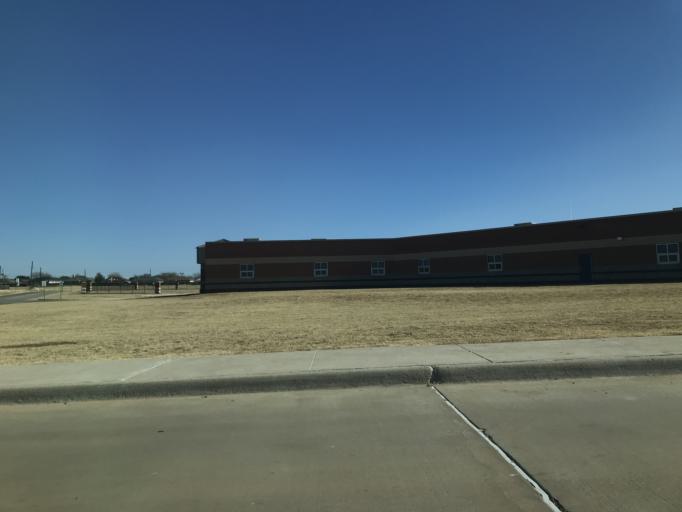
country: US
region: Texas
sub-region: Taylor County
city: Abilene
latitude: 32.4422
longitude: -99.7083
